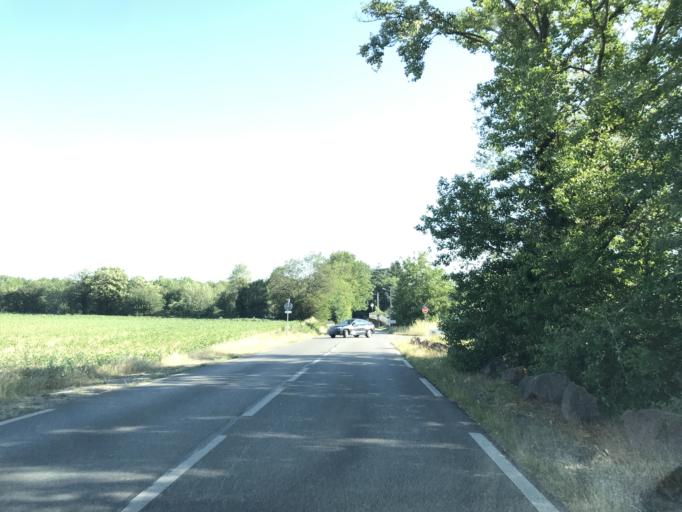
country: FR
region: Rhone-Alpes
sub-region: Departement du Rhone
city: Saint-Bonnet-de-Mure
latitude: 45.6950
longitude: 4.9835
